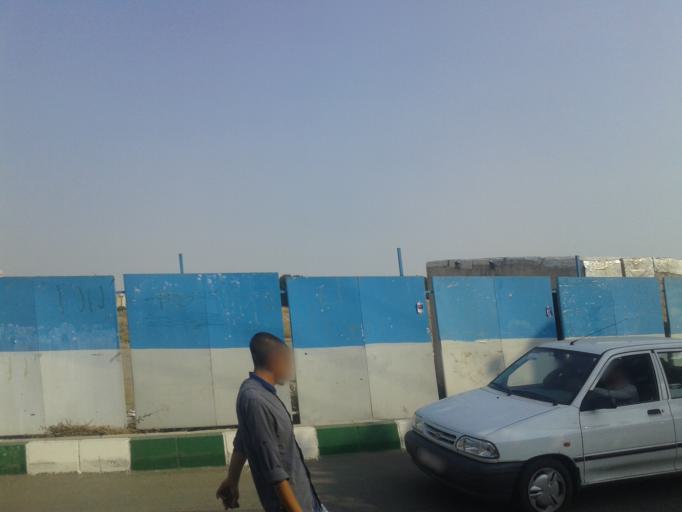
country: IR
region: Tehran
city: Tehran
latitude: 35.6550
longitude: 51.3199
